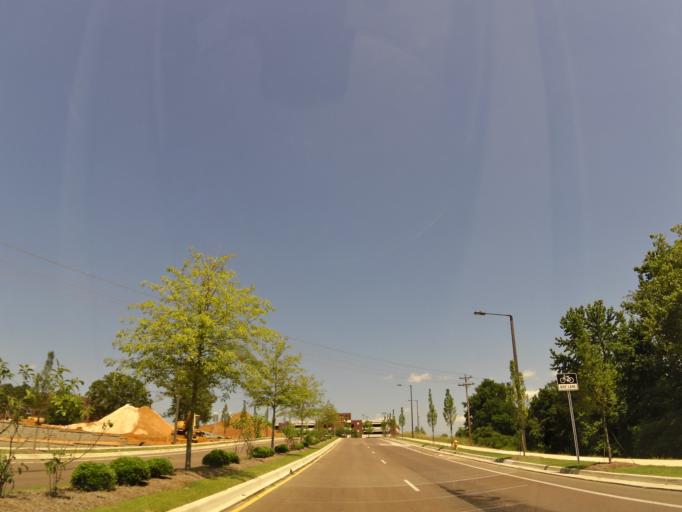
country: US
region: Mississippi
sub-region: Lafayette County
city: University
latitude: 34.3473
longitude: -89.5229
